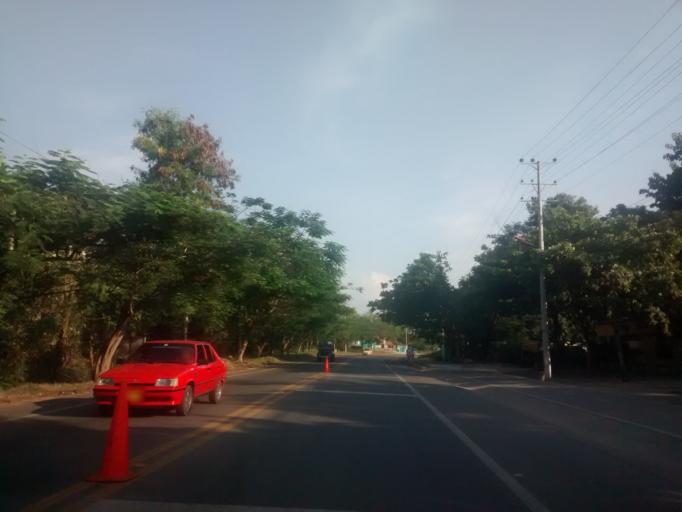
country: CO
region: Cundinamarca
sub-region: Girardot
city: Girardot City
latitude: 4.2988
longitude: -74.7914
